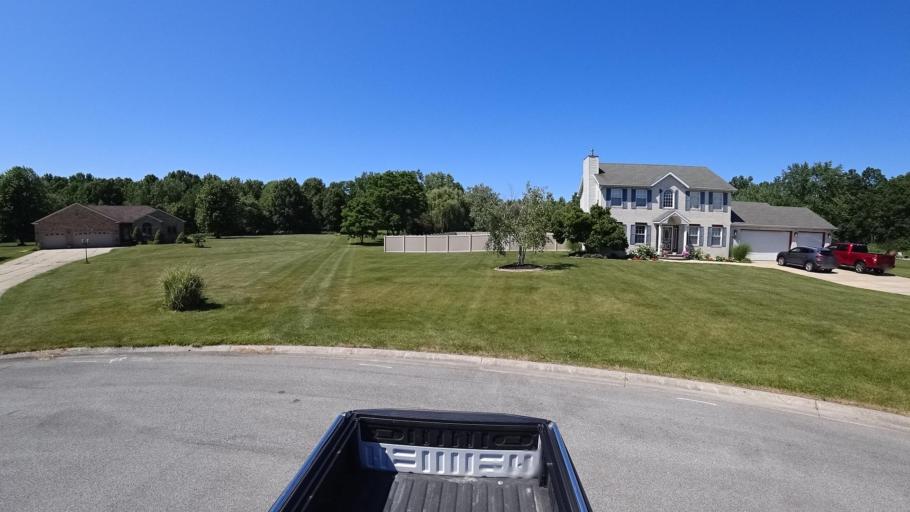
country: US
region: Indiana
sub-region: Porter County
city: Porter
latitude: 41.6030
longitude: -87.0876
